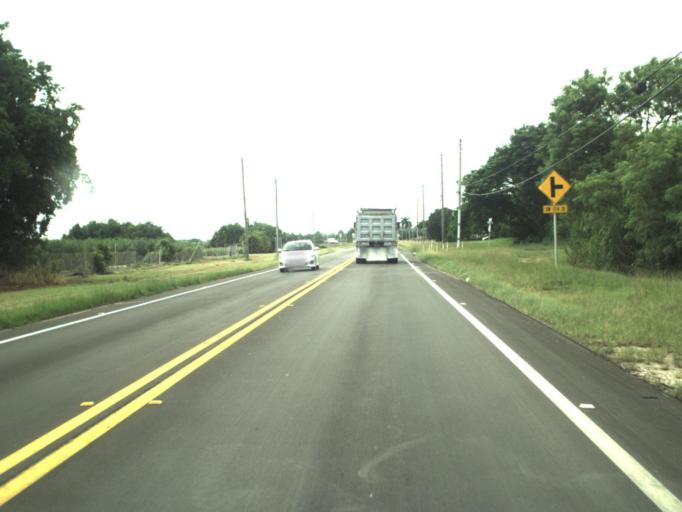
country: US
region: Florida
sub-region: Miami-Dade County
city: Richmond West
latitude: 25.6045
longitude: -80.4789
